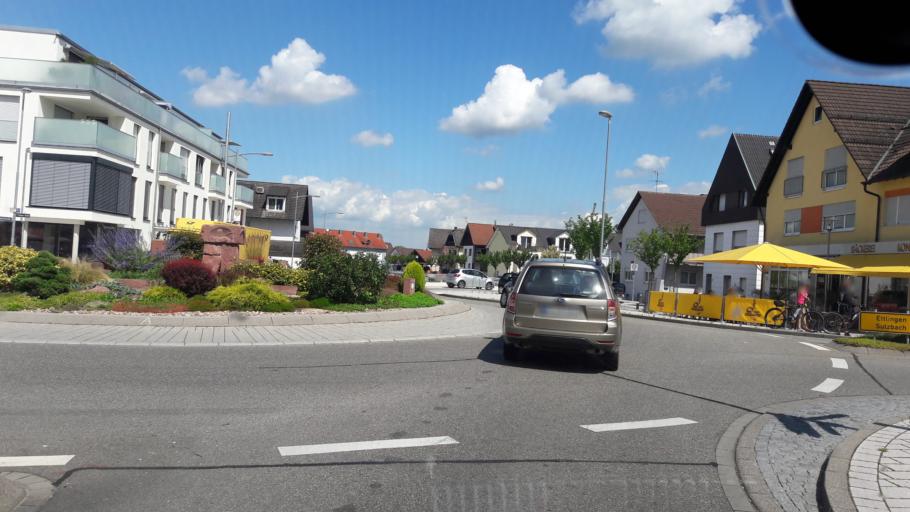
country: DE
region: Baden-Wuerttemberg
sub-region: Karlsruhe Region
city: Malsch
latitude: 48.8836
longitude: 8.3337
